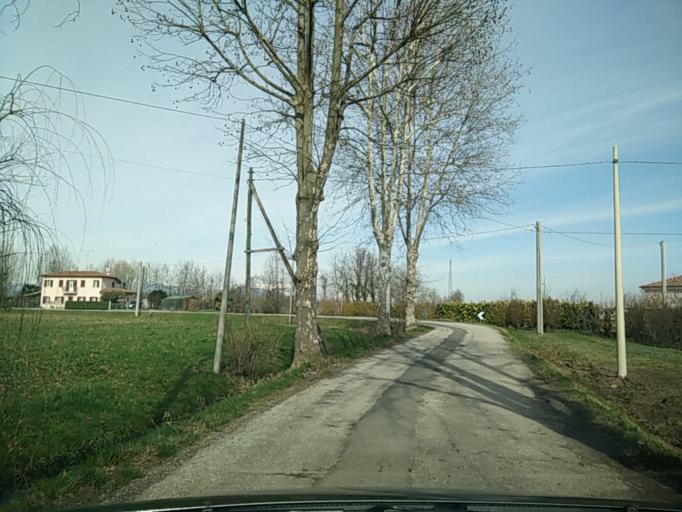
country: IT
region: Veneto
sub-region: Provincia di Treviso
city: Mignagola
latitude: 45.6971
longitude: 12.3188
